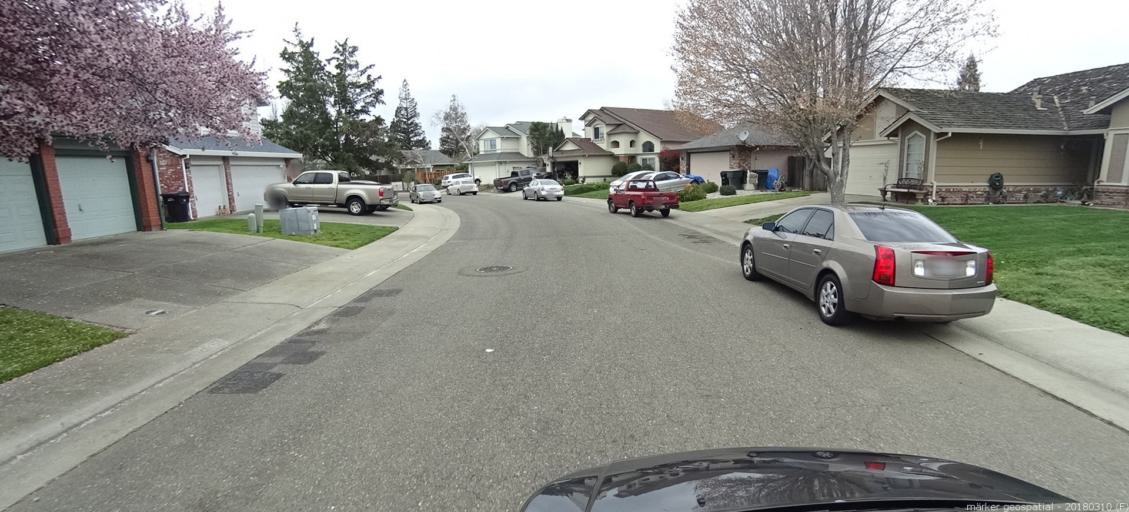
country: US
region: California
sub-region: Sacramento County
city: Vineyard
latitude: 38.4574
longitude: -121.3774
